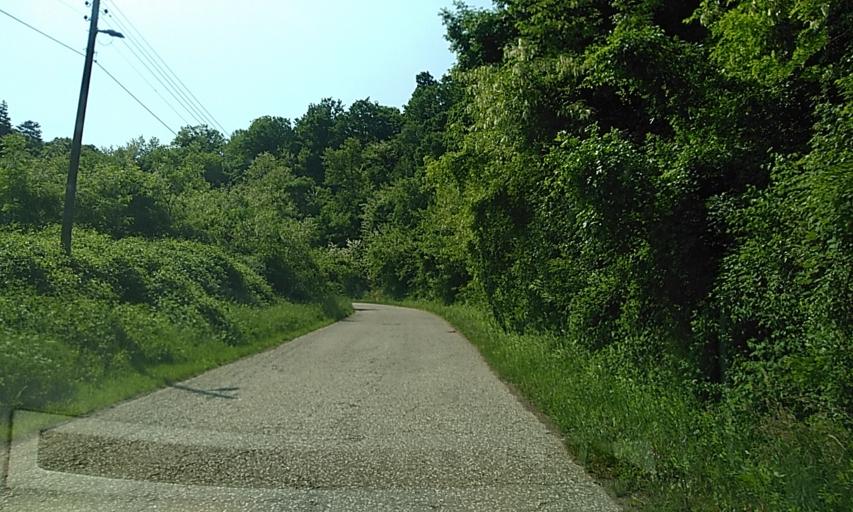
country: RS
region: Central Serbia
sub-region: Pcinjski Okrug
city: Vladicin Han
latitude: 42.7210
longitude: 22.0600
